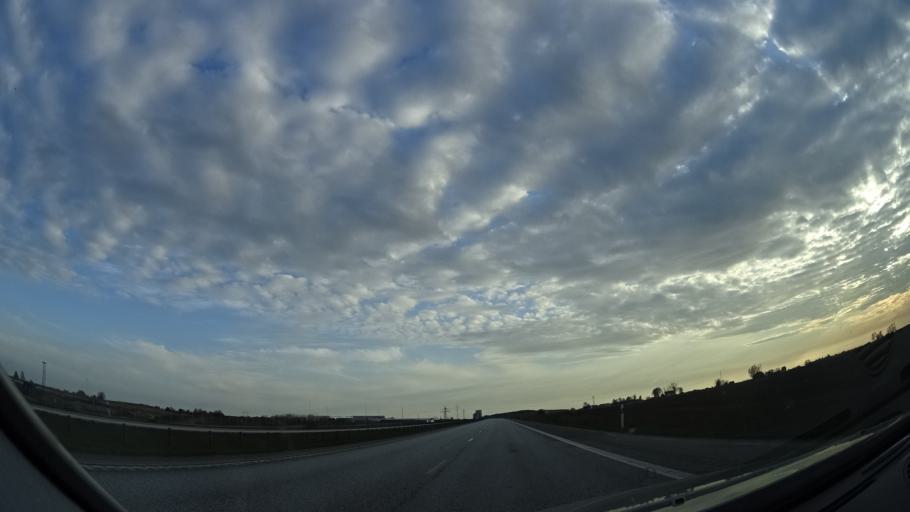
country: SE
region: Skane
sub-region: Lunds Kommun
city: Lund
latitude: 55.7377
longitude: 13.2451
